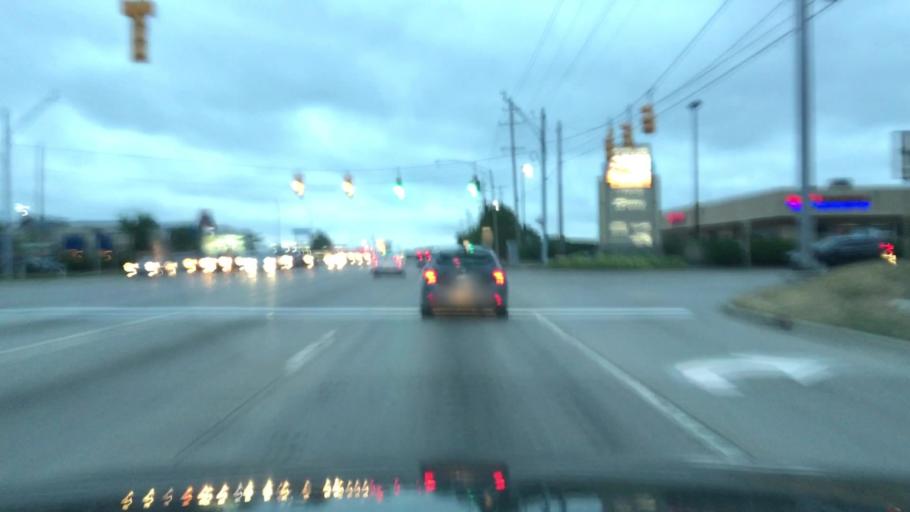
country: US
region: Michigan
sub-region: Kent County
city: East Grand Rapids
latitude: 42.9192
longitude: -85.5840
